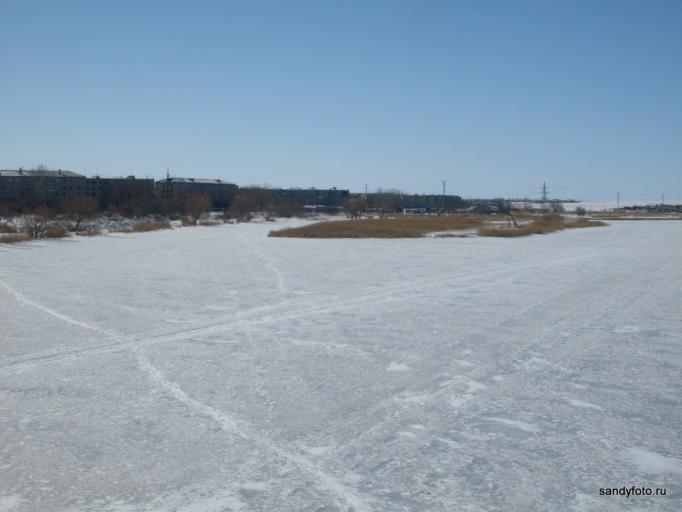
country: RU
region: Chelyabinsk
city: Troitsk
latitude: 54.0925
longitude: 61.5677
